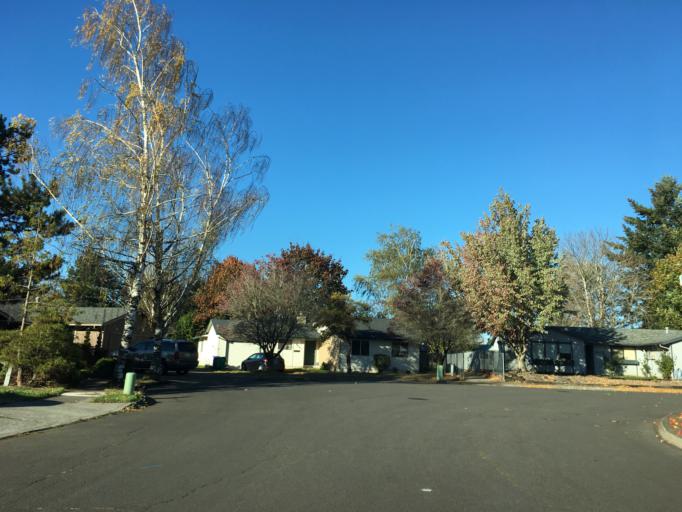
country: US
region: Oregon
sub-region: Multnomah County
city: Wood Village
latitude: 45.5137
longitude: -122.4035
